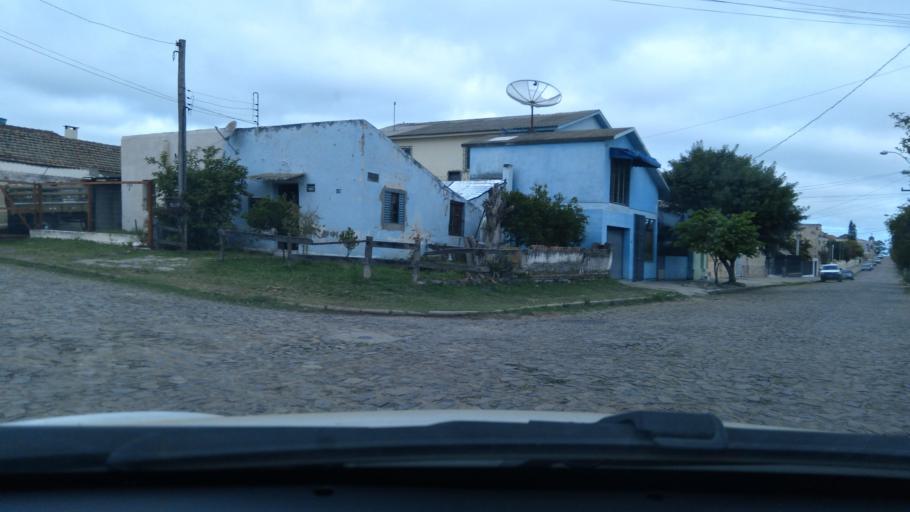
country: BR
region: Rio Grande do Sul
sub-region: Dom Pedrito
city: Dom Pedrito
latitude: -30.9805
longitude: -54.6716
